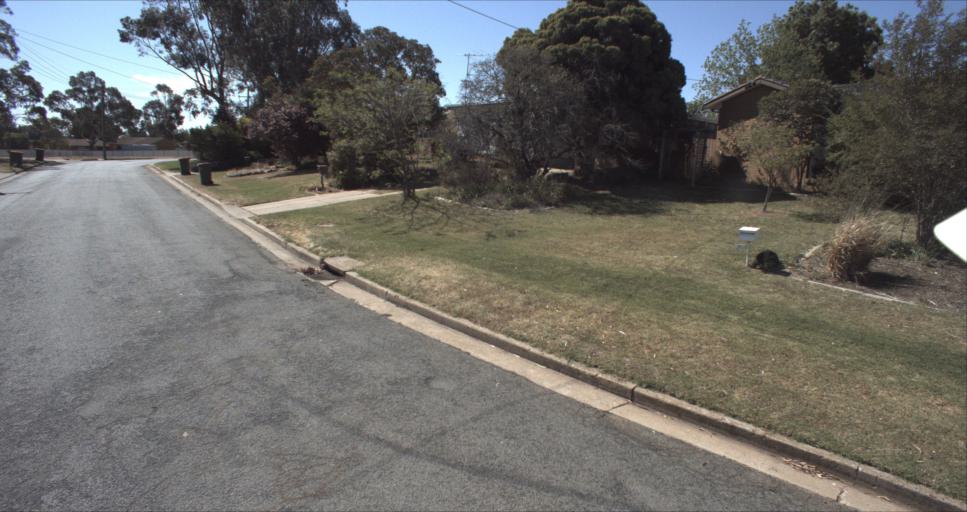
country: AU
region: New South Wales
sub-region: Leeton
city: Leeton
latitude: -34.5514
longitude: 146.3750
